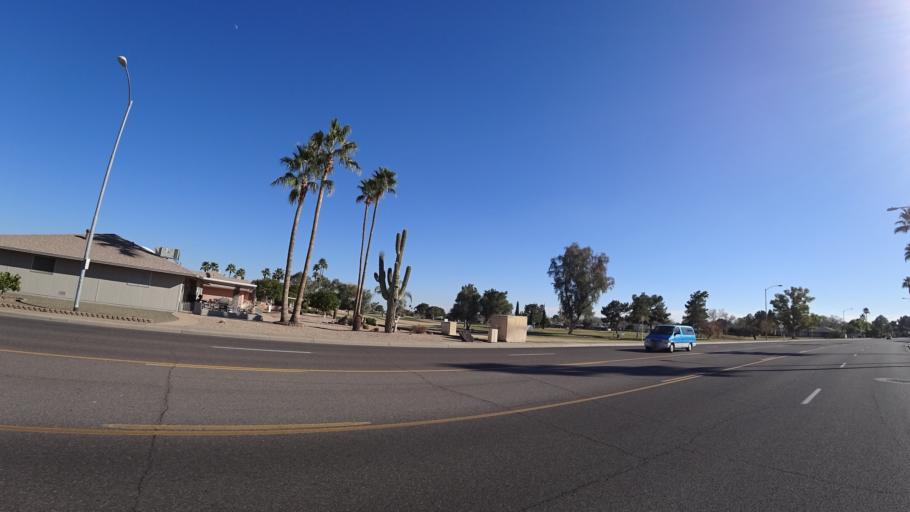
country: US
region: Arizona
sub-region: Maricopa County
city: Sun City West
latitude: 33.6567
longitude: -112.3318
